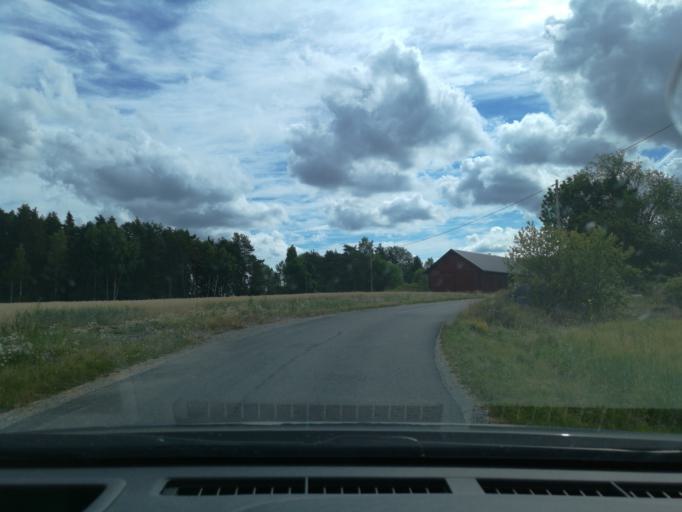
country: SE
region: Stockholm
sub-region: Sigtuna Kommun
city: Marsta
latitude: 59.6649
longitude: 17.8578
